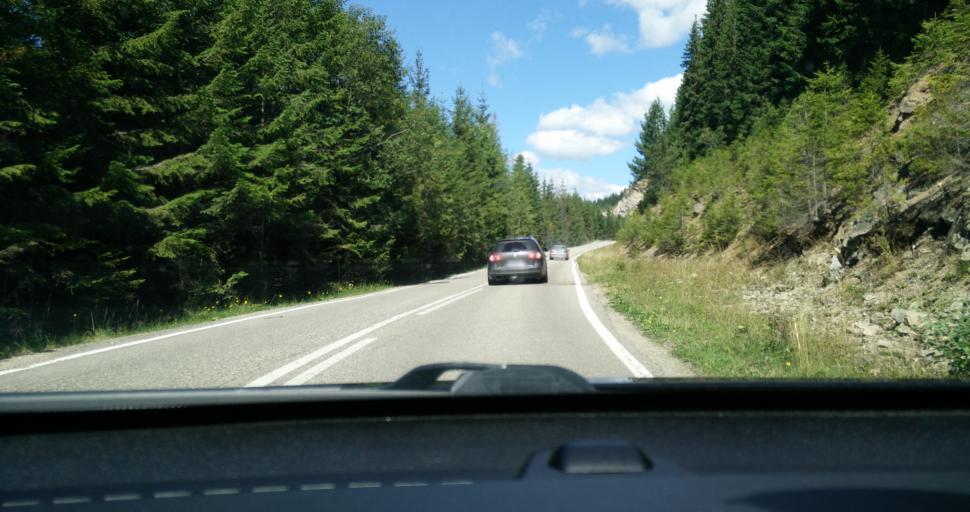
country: RO
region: Alba
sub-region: Comuna Sugag
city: Sugag
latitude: 45.5464
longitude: 23.6344
